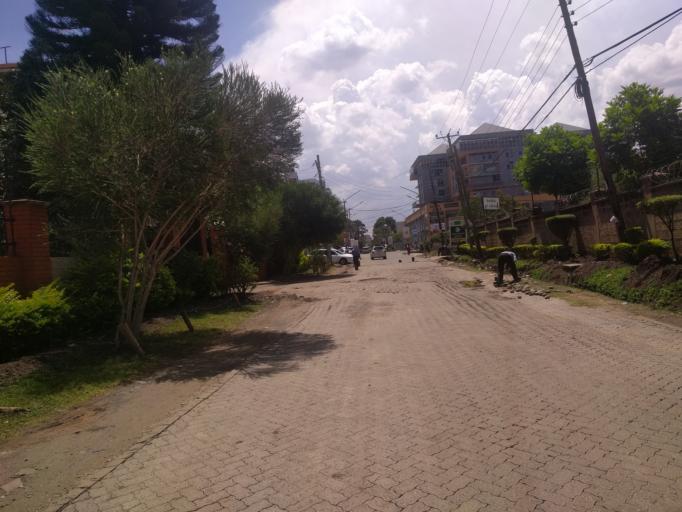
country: KE
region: Nairobi Area
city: Nairobi
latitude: -1.2951
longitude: 36.7888
